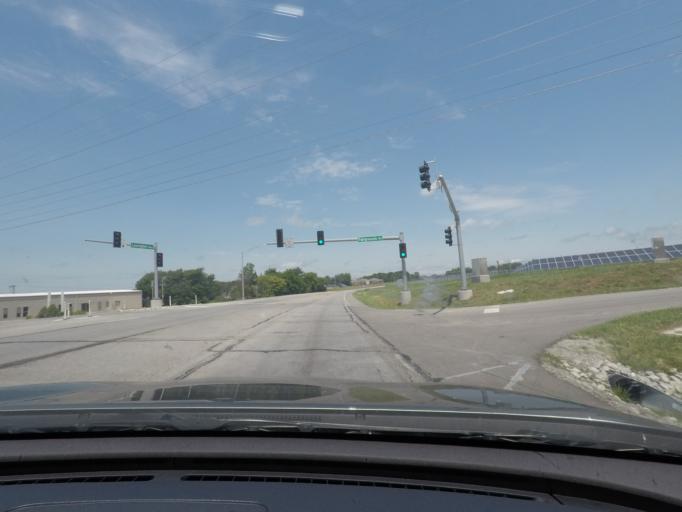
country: US
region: Missouri
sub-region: Saline County
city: Marshall
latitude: 39.0937
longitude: -93.2128
